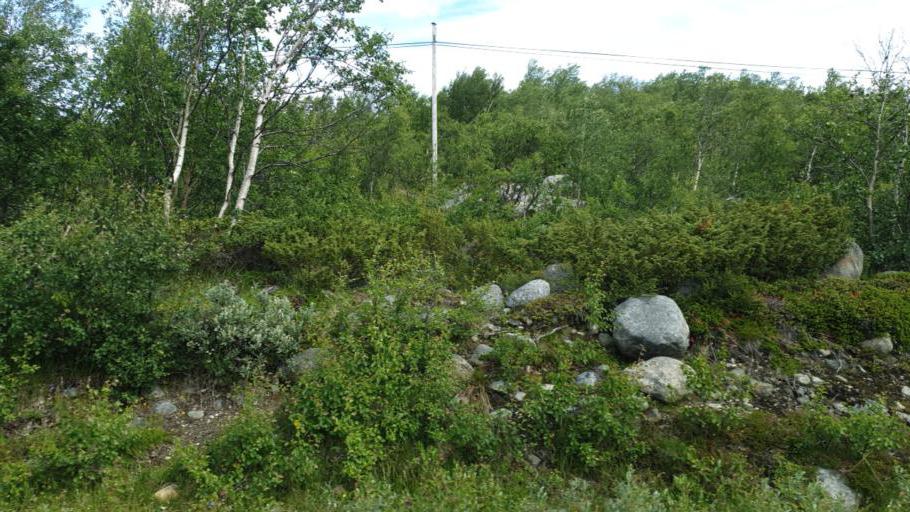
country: NO
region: Oppland
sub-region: Oystre Slidre
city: Heggenes
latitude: 61.4896
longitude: 8.8226
